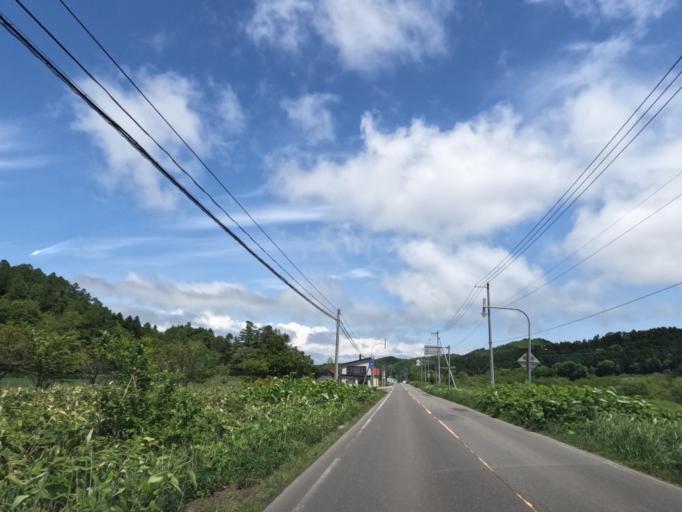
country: JP
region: Hokkaido
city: Tobetsu
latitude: 43.2964
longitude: 141.5420
